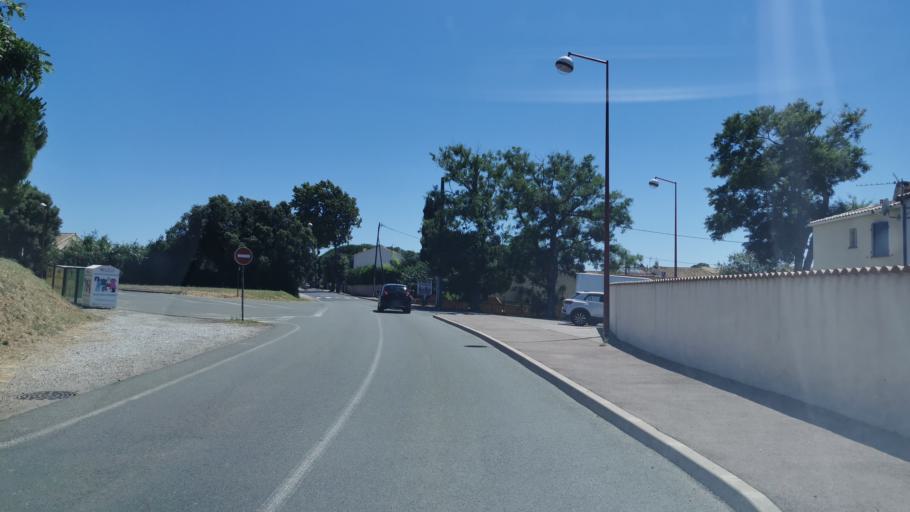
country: FR
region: Languedoc-Roussillon
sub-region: Departement de l'Aude
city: Vinassan
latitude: 43.2072
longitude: 3.0746
